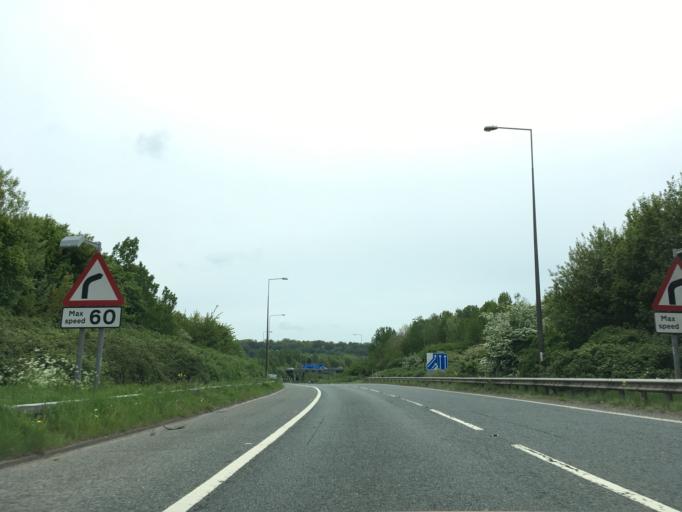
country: GB
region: England
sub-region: North Somerset
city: Easton-in-Gordano
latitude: 51.5043
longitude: -2.6671
